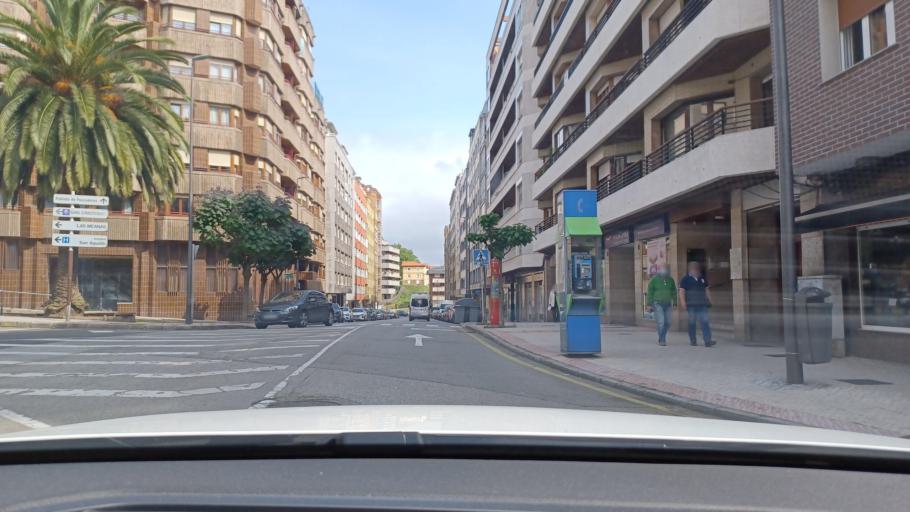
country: ES
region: Asturias
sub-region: Province of Asturias
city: Aviles
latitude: 43.5600
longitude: -5.9255
